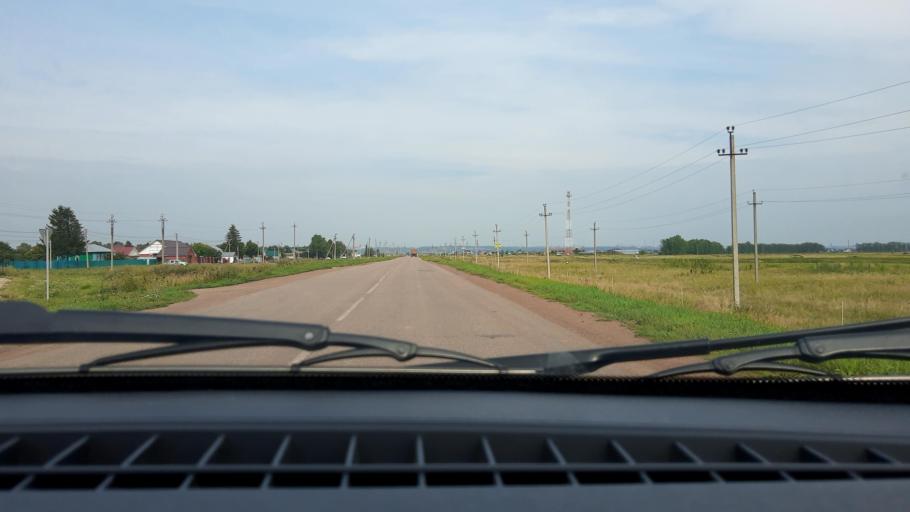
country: RU
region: Bashkortostan
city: Mikhaylovka
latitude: 54.8881
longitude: 55.9041
